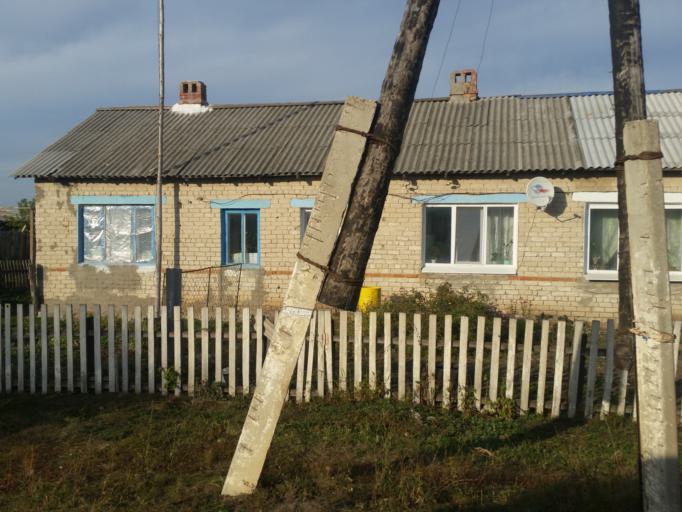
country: RU
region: Ulyanovsk
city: Mullovka
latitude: 54.2657
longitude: 49.1703
